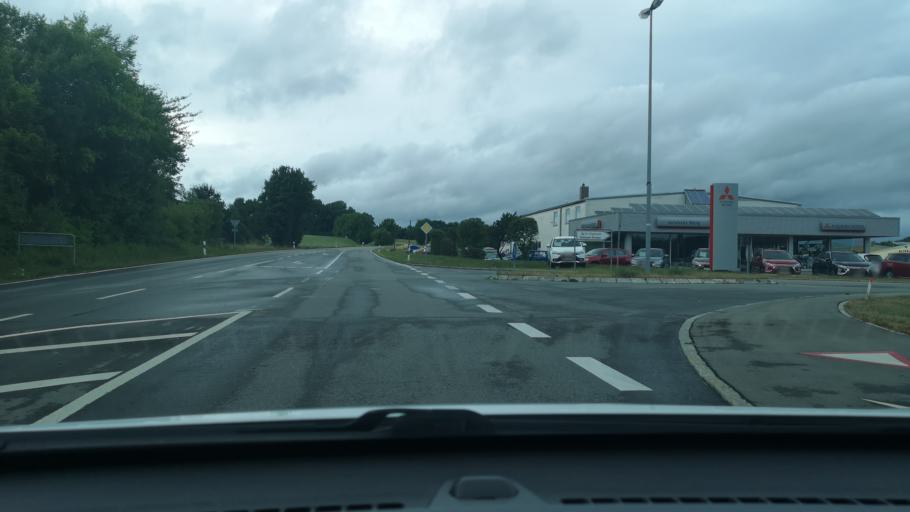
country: DE
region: Baden-Wuerttemberg
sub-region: Freiburg Region
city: Vohringen
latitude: 48.2992
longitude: 8.6266
